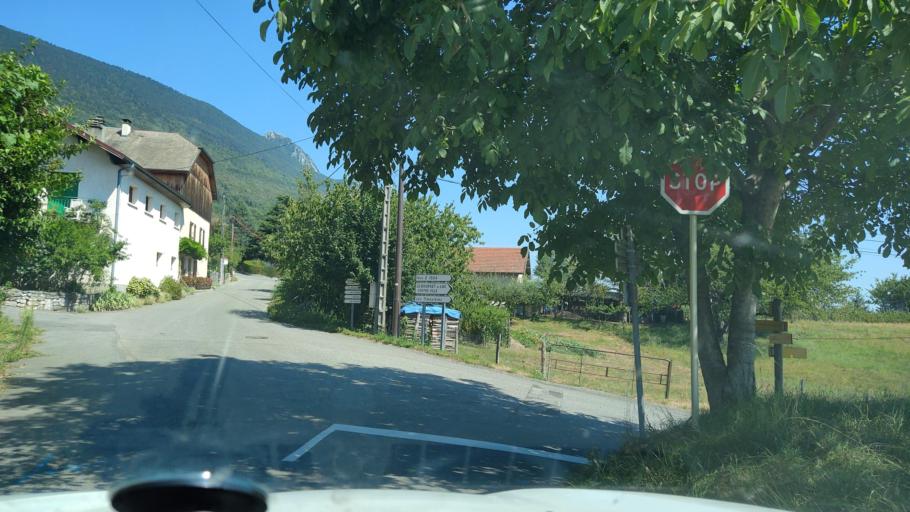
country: FR
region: Rhone-Alpes
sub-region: Departement de la Savoie
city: Le Bourget-du-Lac
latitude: 45.6393
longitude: 5.8493
